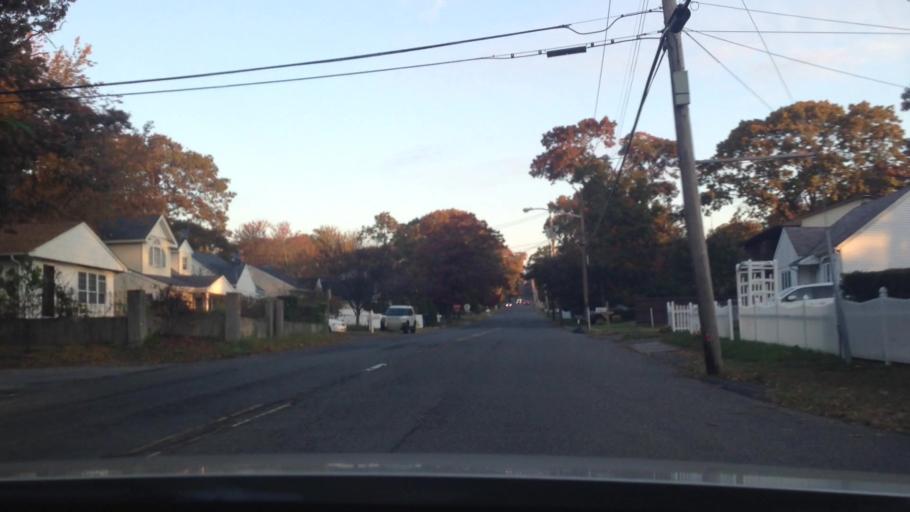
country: US
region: New York
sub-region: Suffolk County
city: Farmingville
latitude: 40.8335
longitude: -73.0342
